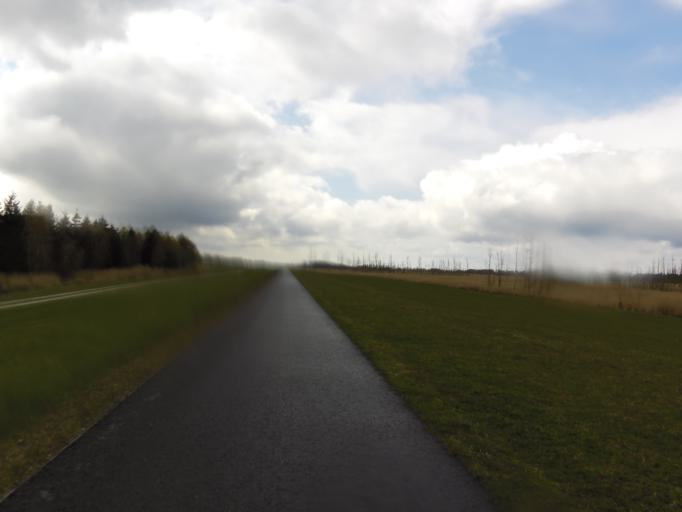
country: DE
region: Mecklenburg-Vorpommern
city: Altenpleen
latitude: 54.4314
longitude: 12.8552
